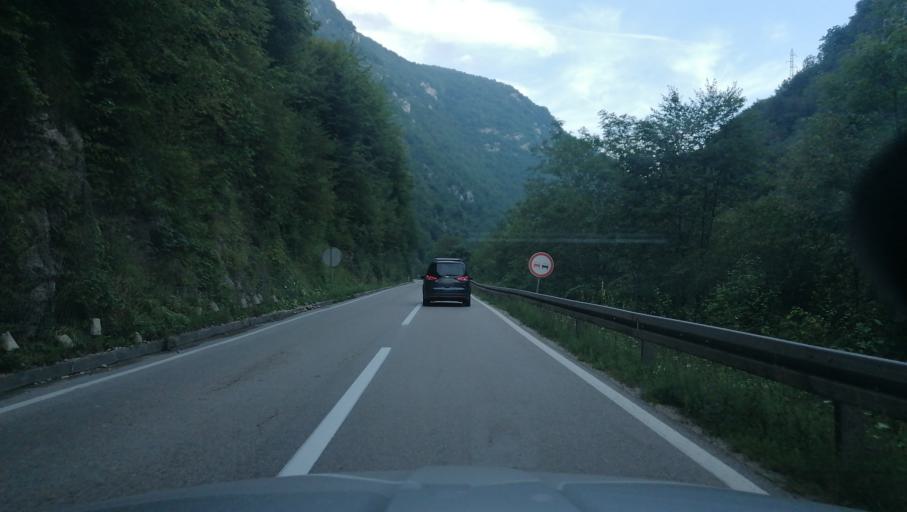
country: BA
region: Federation of Bosnia and Herzegovina
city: Jajce
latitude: 44.4343
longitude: 17.2360
